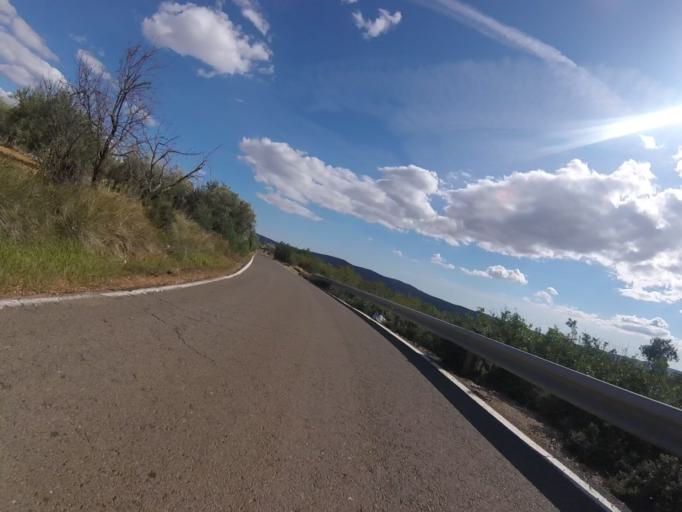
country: ES
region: Valencia
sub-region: Provincia de Castello
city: Cuevas de Vinroma
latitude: 40.3796
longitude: 0.1077
